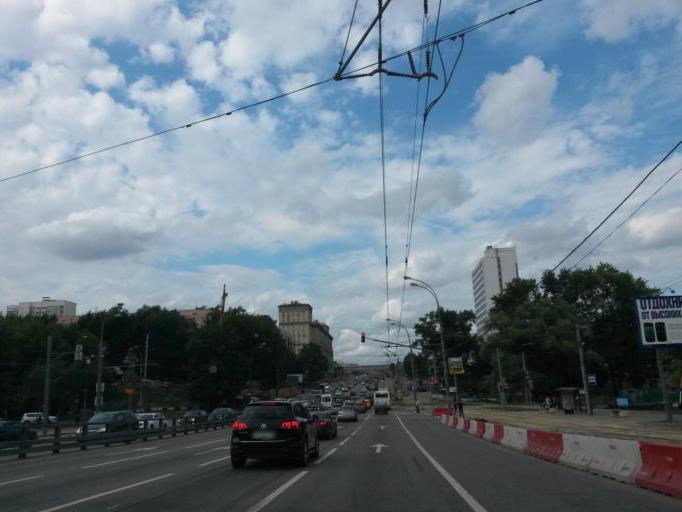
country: RU
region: Moscow
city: Kotlovka
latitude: 55.6896
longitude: 37.6223
